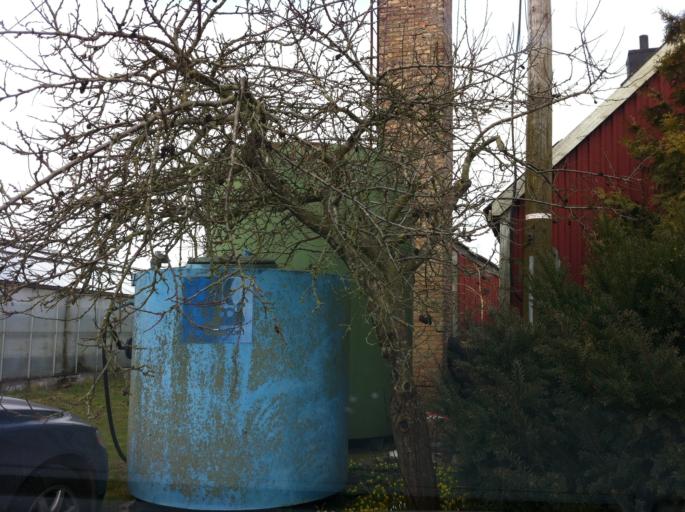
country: SE
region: Skane
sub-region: Svalovs Kommun
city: Teckomatorp
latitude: 55.8551
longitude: 13.0845
